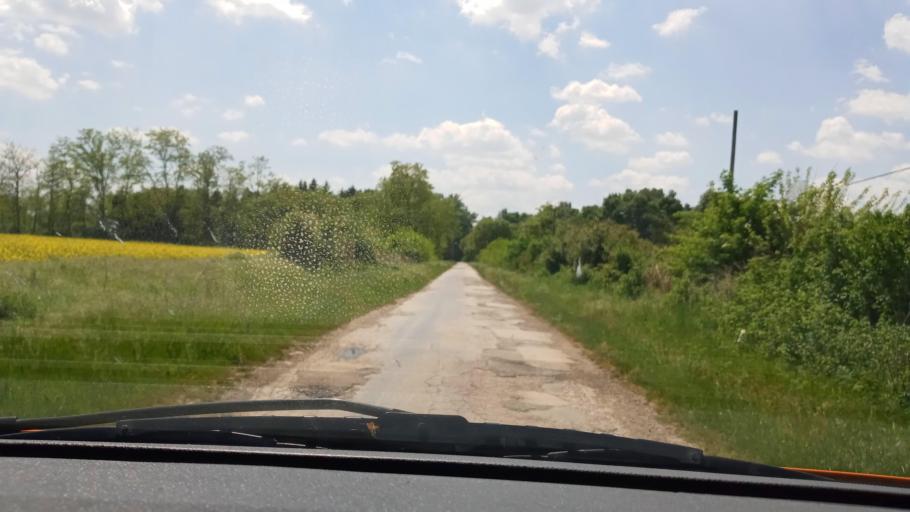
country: HU
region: Baranya
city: Siklos
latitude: 45.7744
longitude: 18.2754
